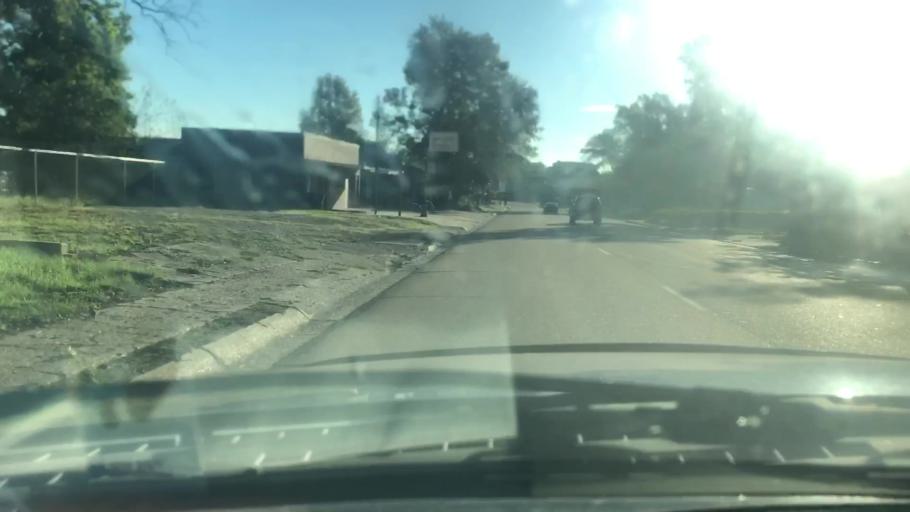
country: US
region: Texas
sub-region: Bowie County
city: Texarkana
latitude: 33.4233
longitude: -94.0563
